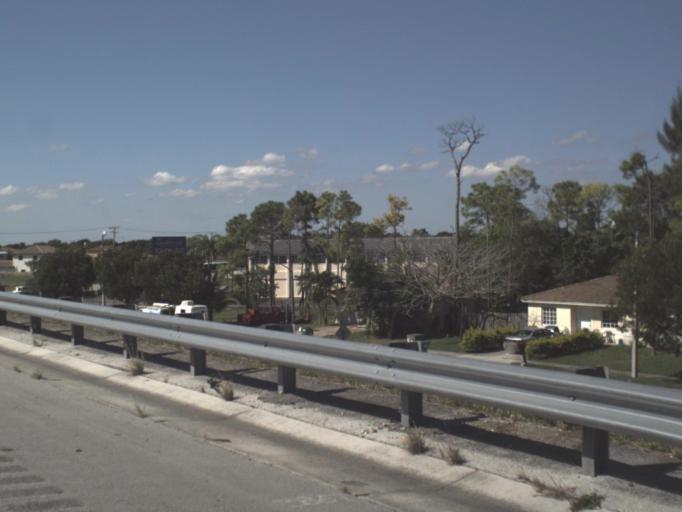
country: US
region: Florida
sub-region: Miami-Dade County
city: Naranja
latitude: 25.5190
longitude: -80.4043
